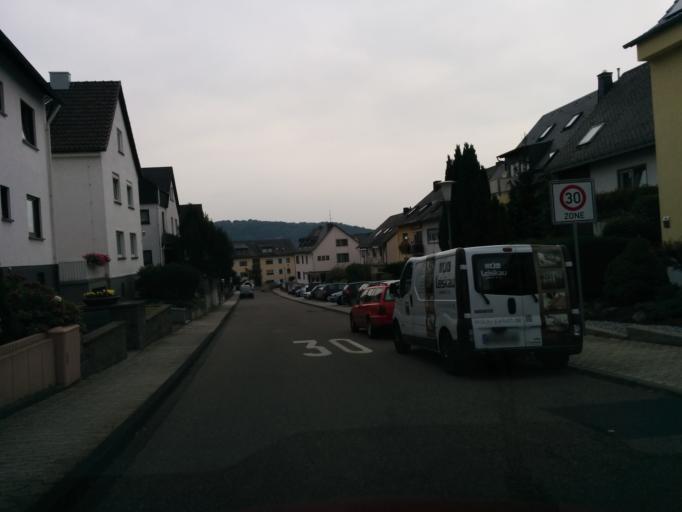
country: DE
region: Rheinland-Pfalz
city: Lahnstein
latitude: 50.3262
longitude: 7.6034
